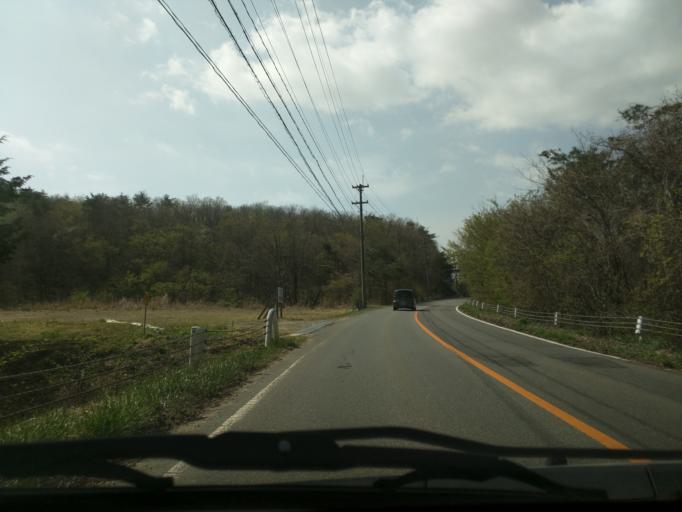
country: JP
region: Fukushima
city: Nihommatsu
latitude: 37.5989
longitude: 140.3624
